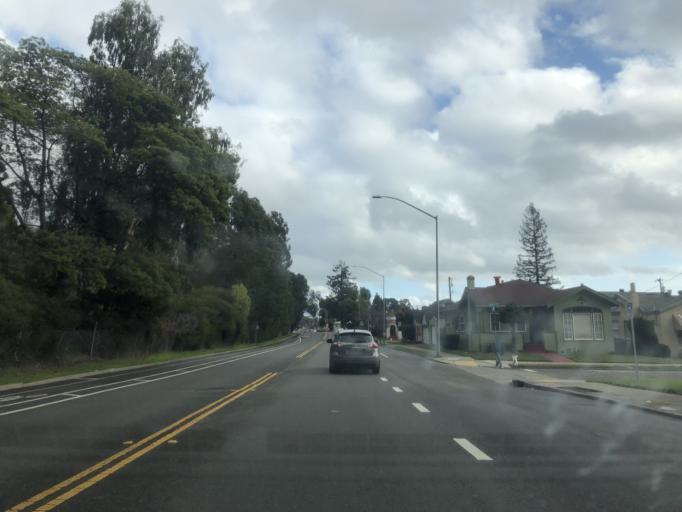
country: US
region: California
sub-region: Alameda County
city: Alameda
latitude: 37.7771
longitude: -122.1873
